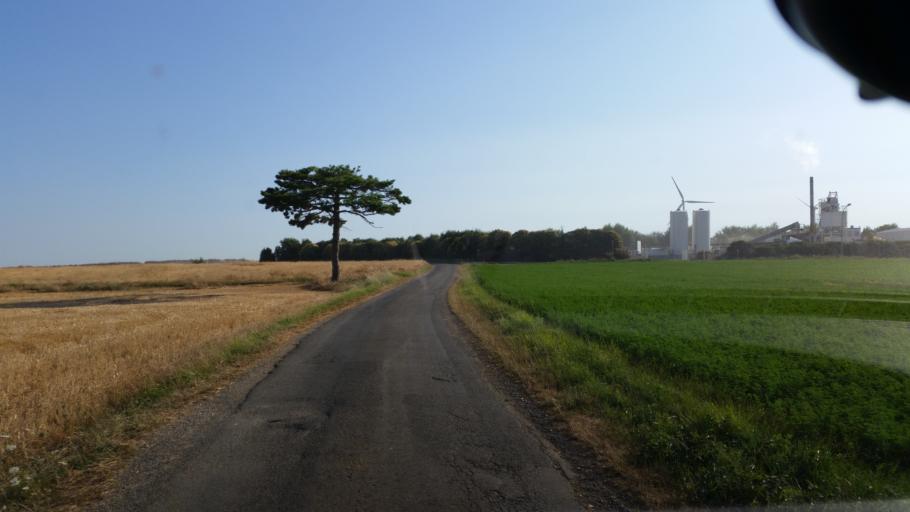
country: FR
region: Poitou-Charentes
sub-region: Departement de la Charente-Maritime
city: Saint-Jean-de-Liversay
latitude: 46.2329
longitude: -0.8898
